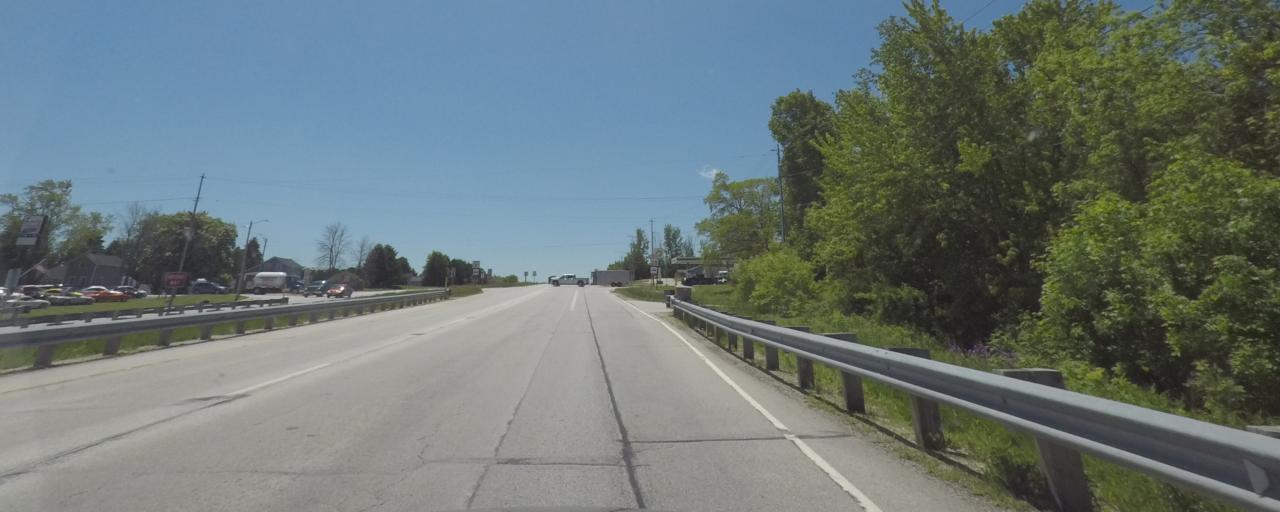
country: US
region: Wisconsin
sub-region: Sheboygan County
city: Plymouth
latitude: 43.6756
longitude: -87.9410
